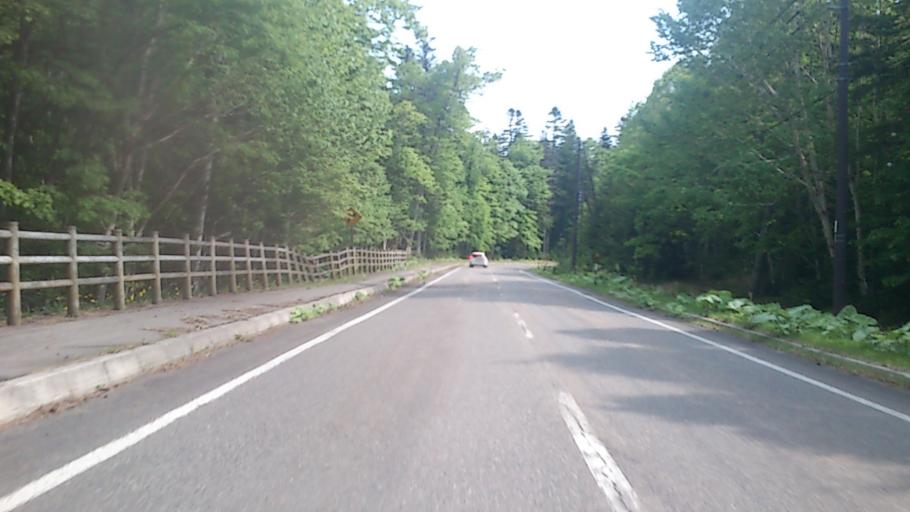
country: JP
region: Hokkaido
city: Kitami
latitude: 43.3918
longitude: 143.9712
